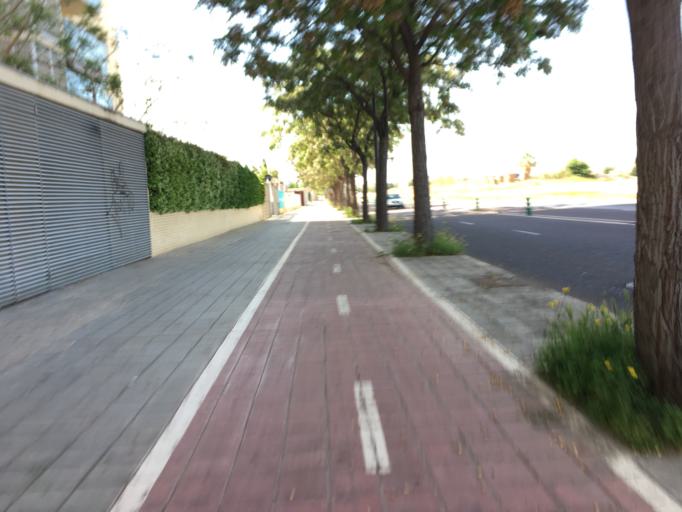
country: ES
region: Valencia
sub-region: Provincia de Valencia
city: Mislata
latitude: 39.4863
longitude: -0.4053
